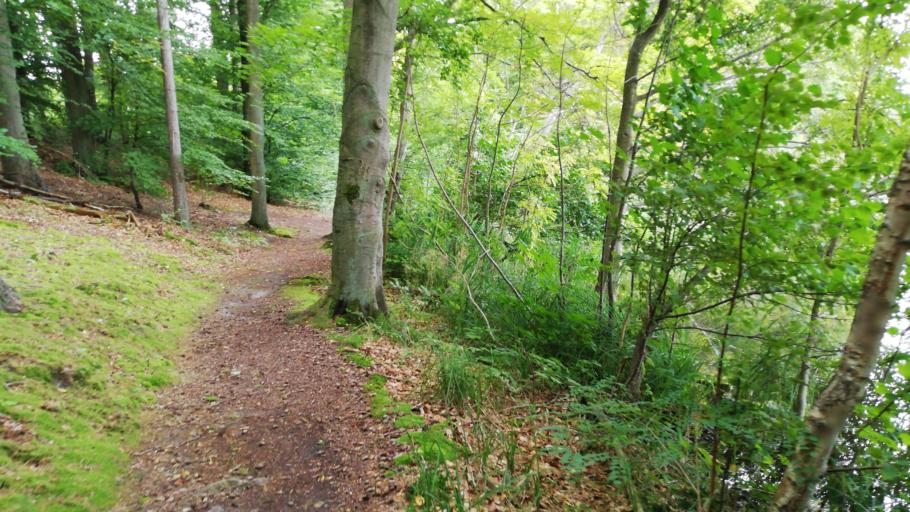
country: DE
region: Brandenburg
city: Rheinsberg
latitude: 53.1017
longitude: 12.8758
